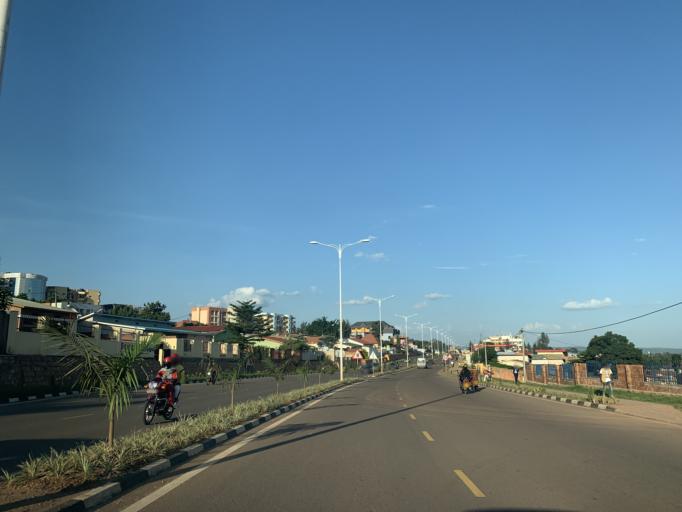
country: RW
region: Kigali
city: Kigali
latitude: -1.9625
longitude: 30.1097
